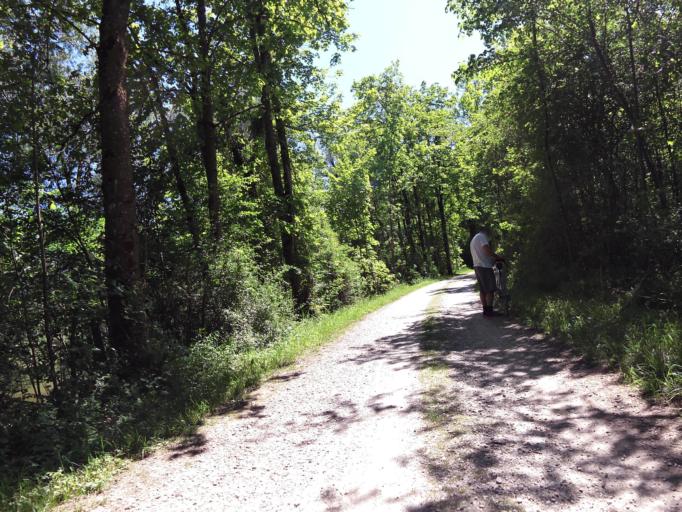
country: DE
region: Bavaria
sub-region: Upper Bavaria
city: Ismaning
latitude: 48.2533
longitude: 11.6835
